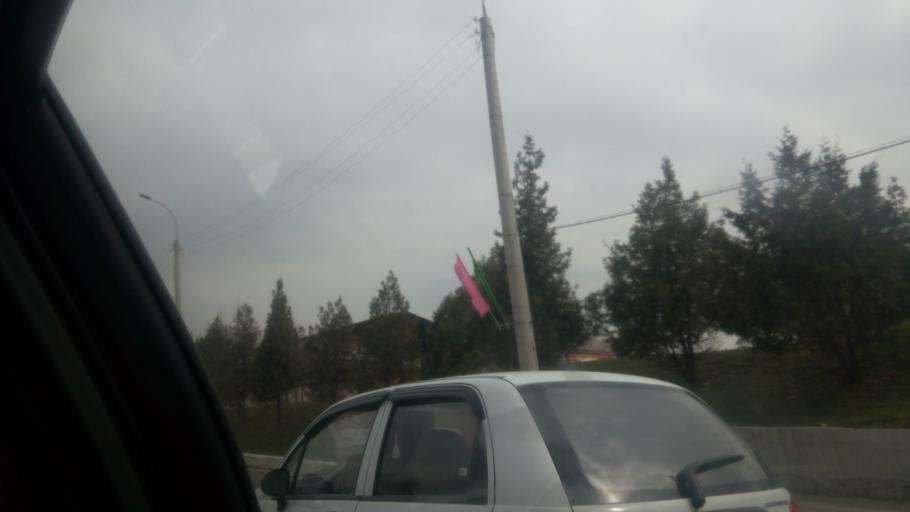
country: UZ
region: Toshkent
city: Salor
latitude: 41.3349
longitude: 69.3113
